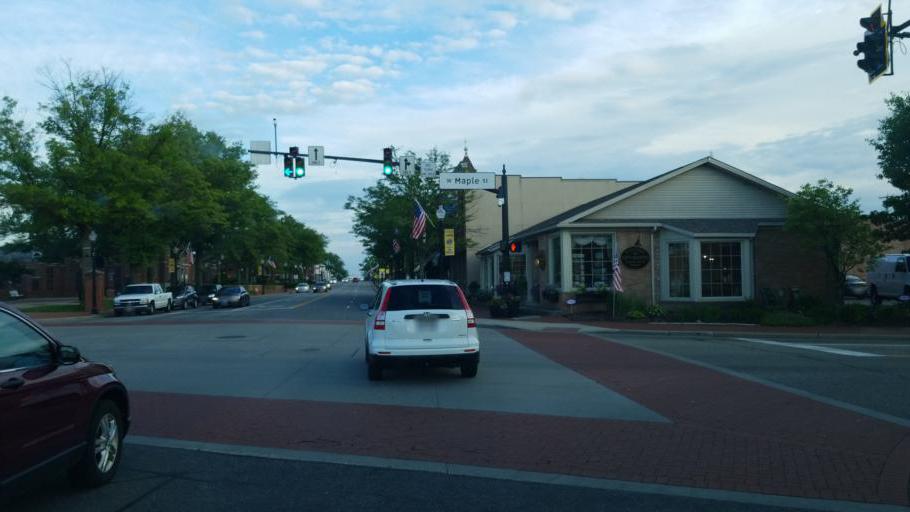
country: US
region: Ohio
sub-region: Stark County
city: North Canton
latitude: 40.8760
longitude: -81.4024
